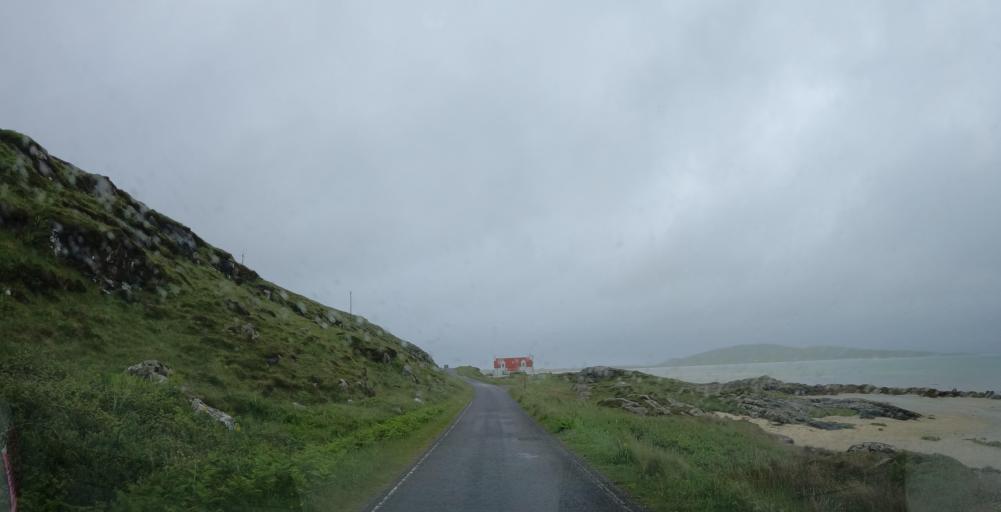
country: GB
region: Scotland
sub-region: Eilean Siar
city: Barra
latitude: 57.0160
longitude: -7.4342
